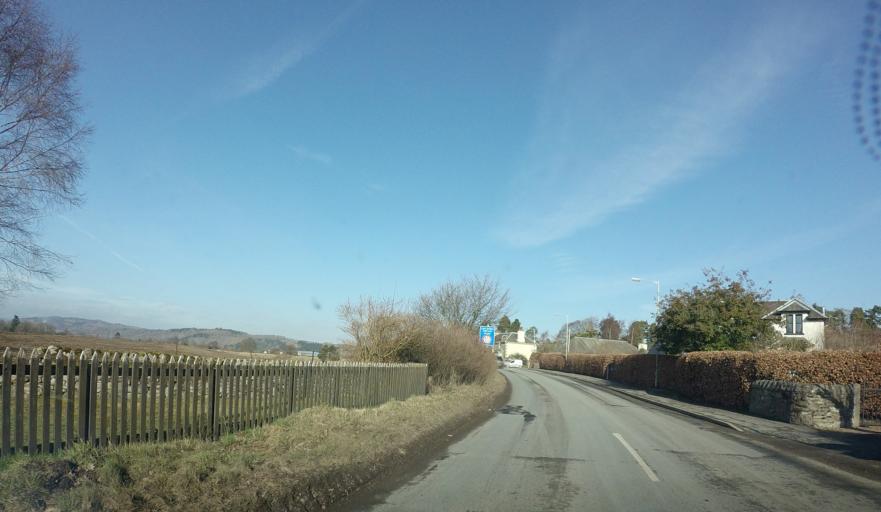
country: GB
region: Scotland
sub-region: Perth and Kinross
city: Bankfoot
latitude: 56.5286
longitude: -3.4665
